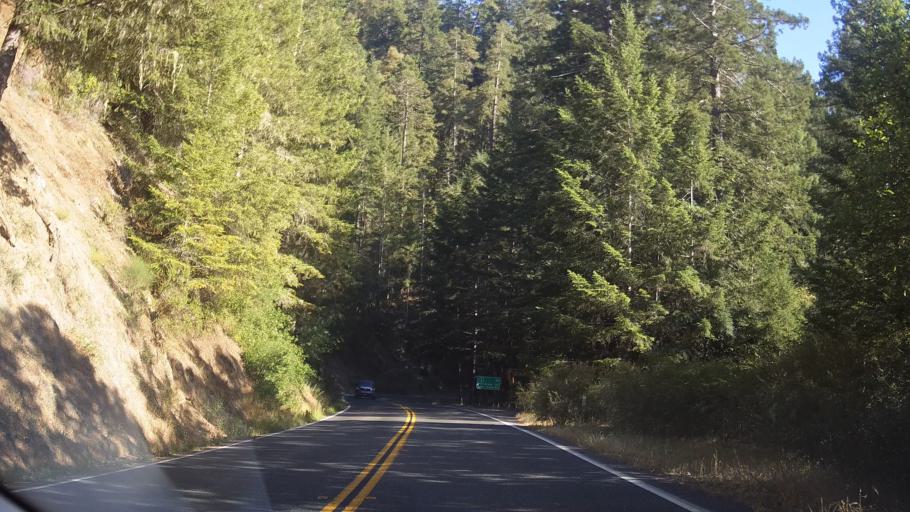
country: US
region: California
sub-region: Mendocino County
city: Brooktrails
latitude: 39.3672
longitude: -123.4988
